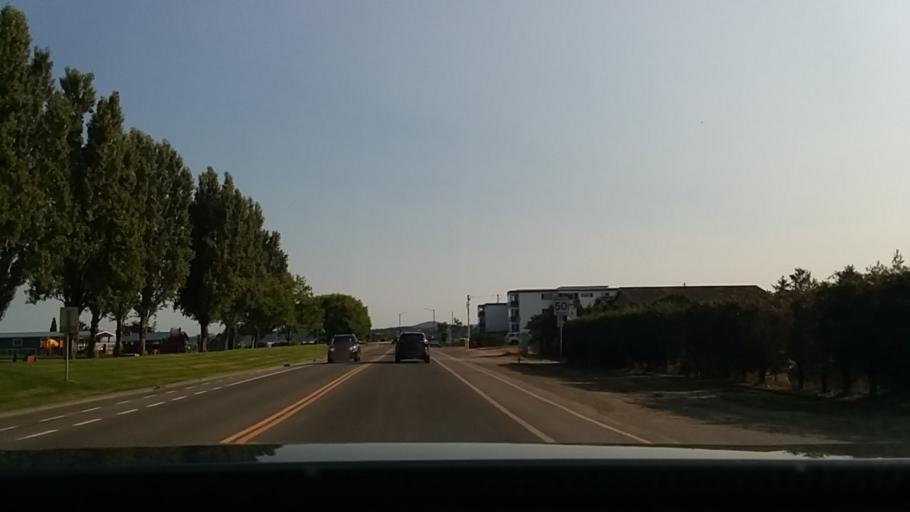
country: CA
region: British Columbia
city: North Saanich
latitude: 48.6434
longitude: -123.4004
